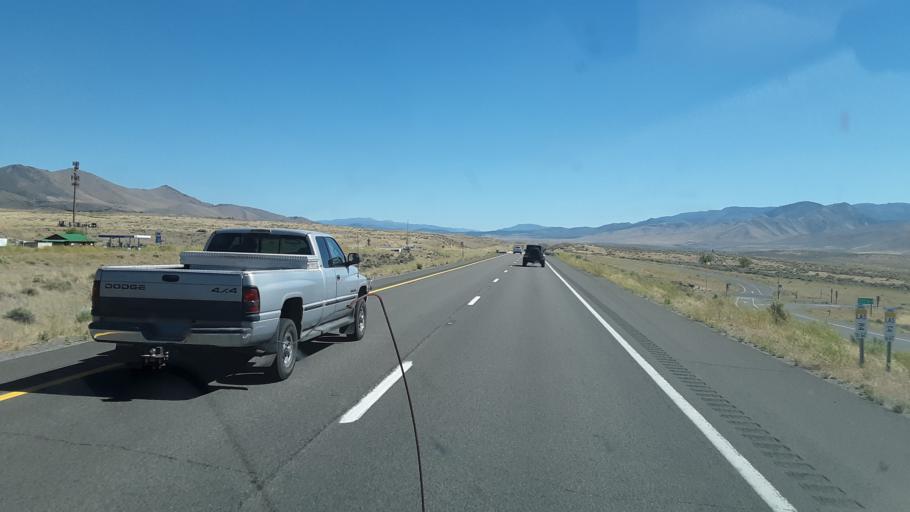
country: US
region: Nevada
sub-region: Washoe County
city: Cold Springs
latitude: 39.7776
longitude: -120.0390
